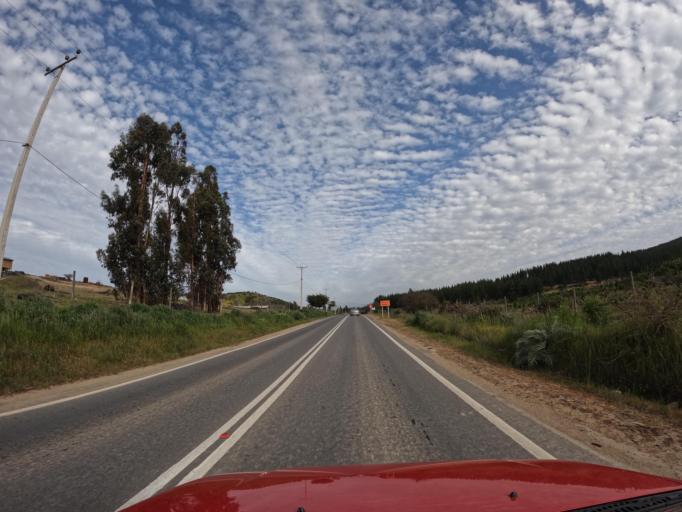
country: CL
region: O'Higgins
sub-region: Provincia de Colchagua
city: Santa Cruz
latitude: -34.3200
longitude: -71.7612
